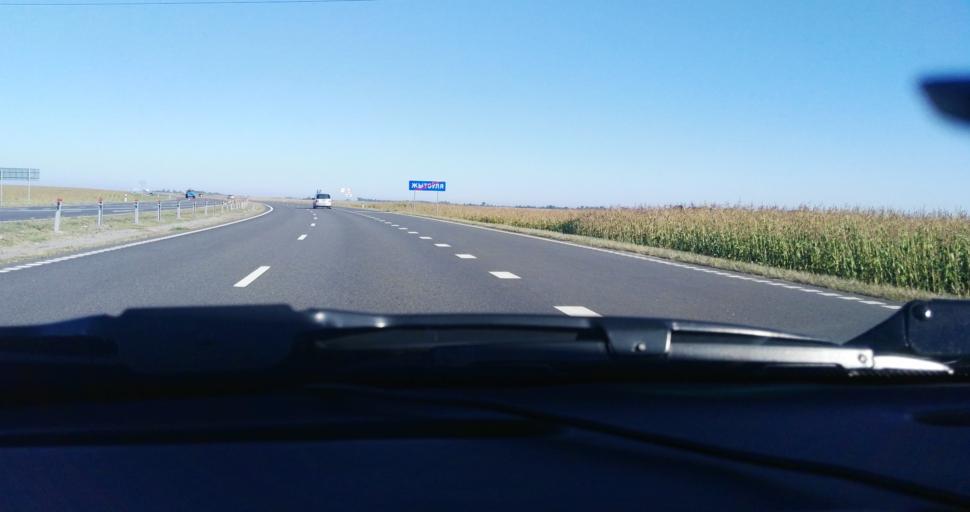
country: BY
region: Gomel
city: Buda-Kashalyova
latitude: 52.5207
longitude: 30.6257
